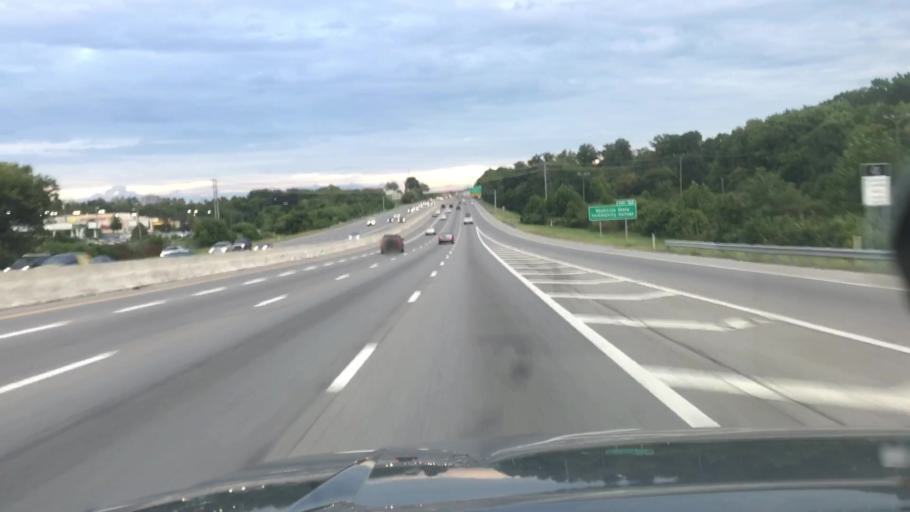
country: US
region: Tennessee
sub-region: Rutherford County
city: La Vergne
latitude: 36.0441
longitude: -86.6571
